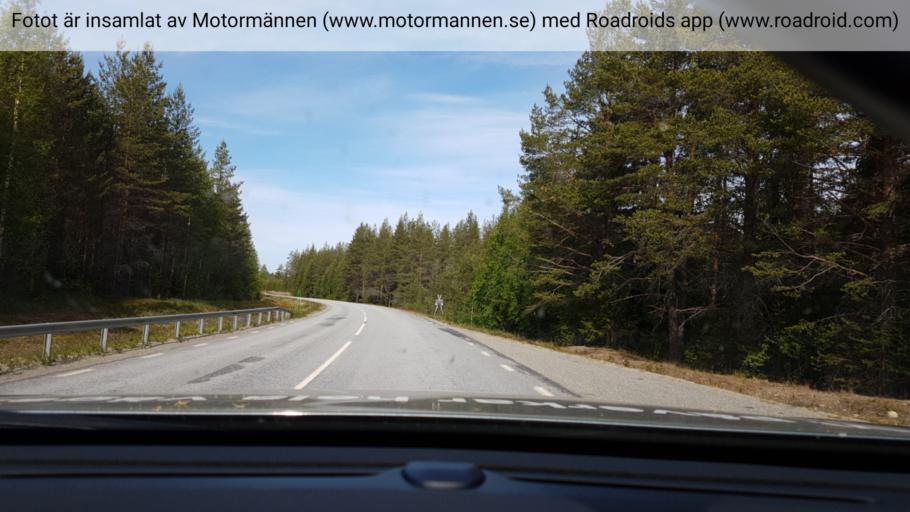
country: SE
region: Vaesterbotten
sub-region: Asele Kommun
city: Asele
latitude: 64.2064
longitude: 17.0103
